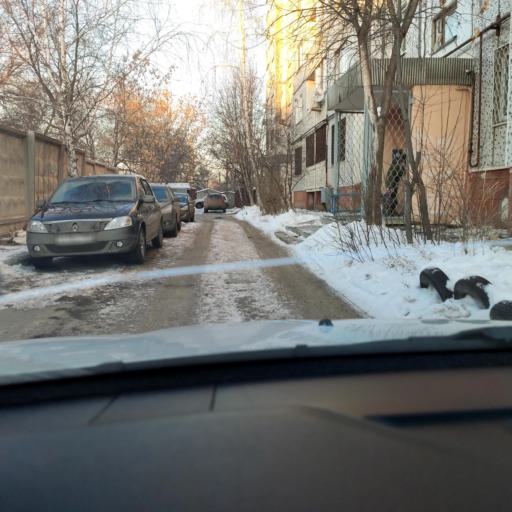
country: RU
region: Samara
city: Samara
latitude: 53.2583
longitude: 50.1844
